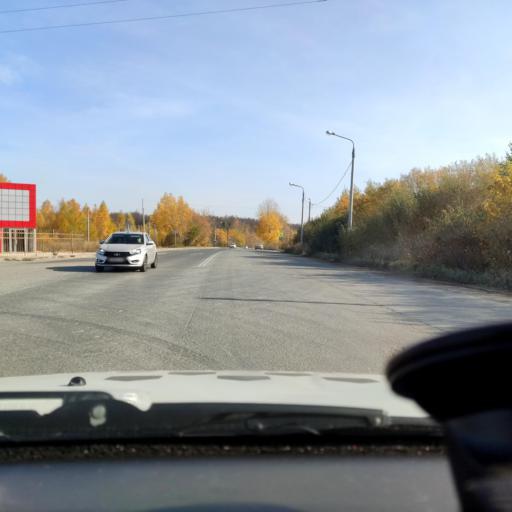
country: RU
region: Perm
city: Froly
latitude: 57.9562
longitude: 56.2877
